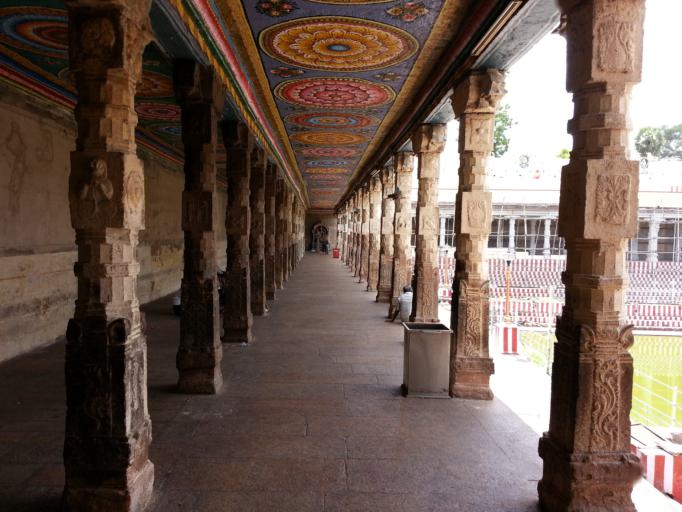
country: IN
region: Tamil Nadu
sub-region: Madurai
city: Madurai
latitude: 9.9200
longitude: 78.1197
